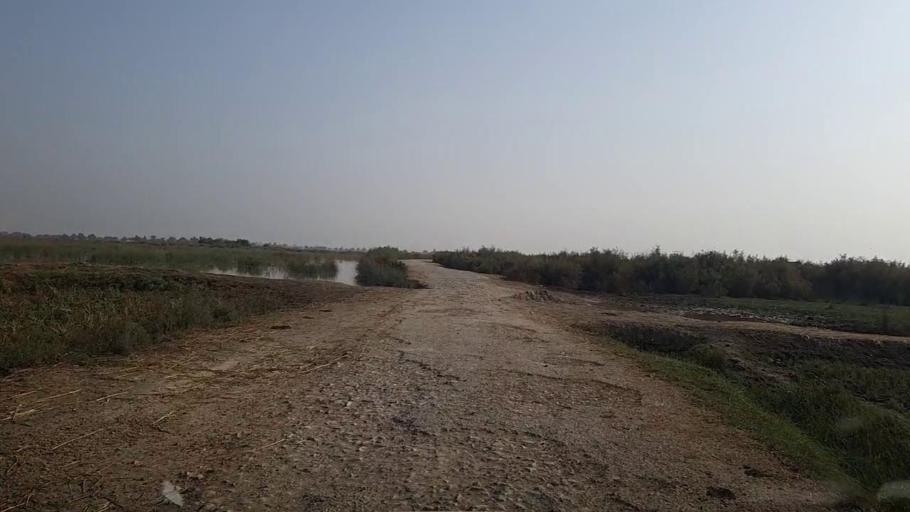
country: PK
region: Sindh
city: Kandhkot
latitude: 28.2958
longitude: 69.2526
